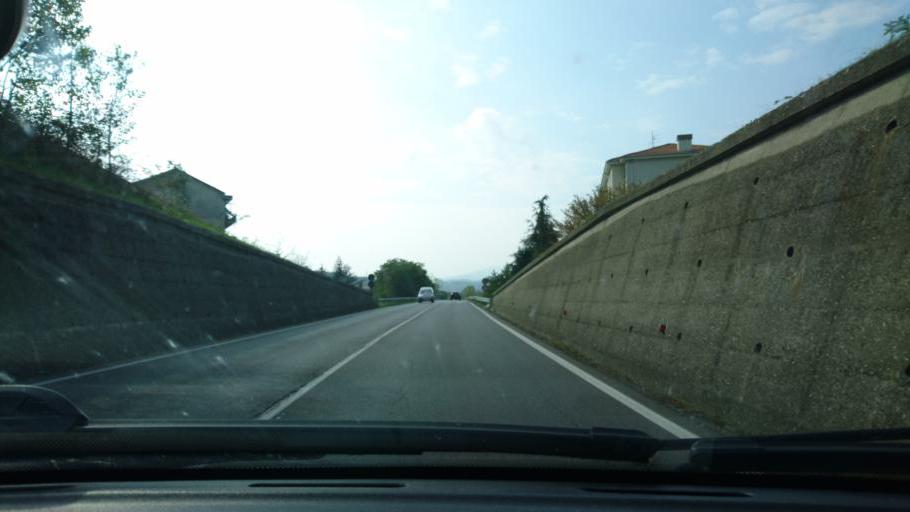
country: IT
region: Liguria
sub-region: Provincia di Savona
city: Cairo Montenotte
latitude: 44.4000
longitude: 8.2839
